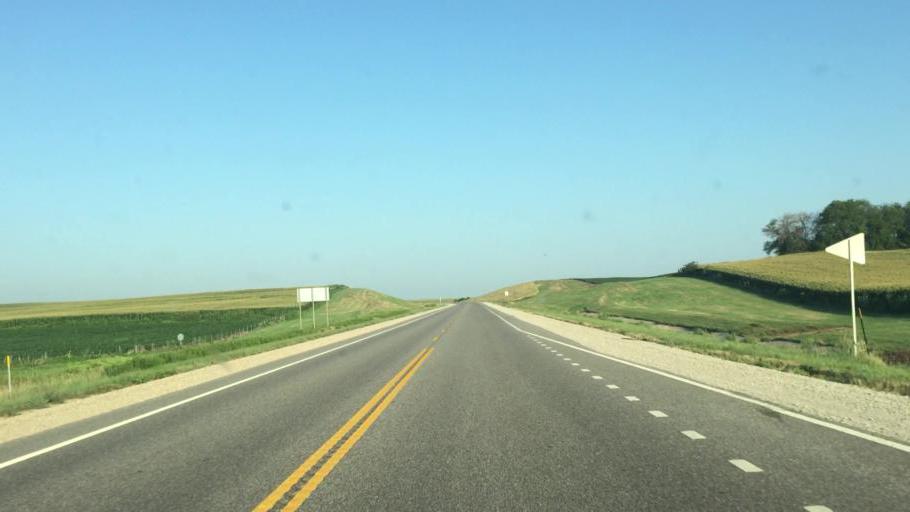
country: US
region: Kansas
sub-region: Doniphan County
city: Highland
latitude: 39.8410
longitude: -95.2721
